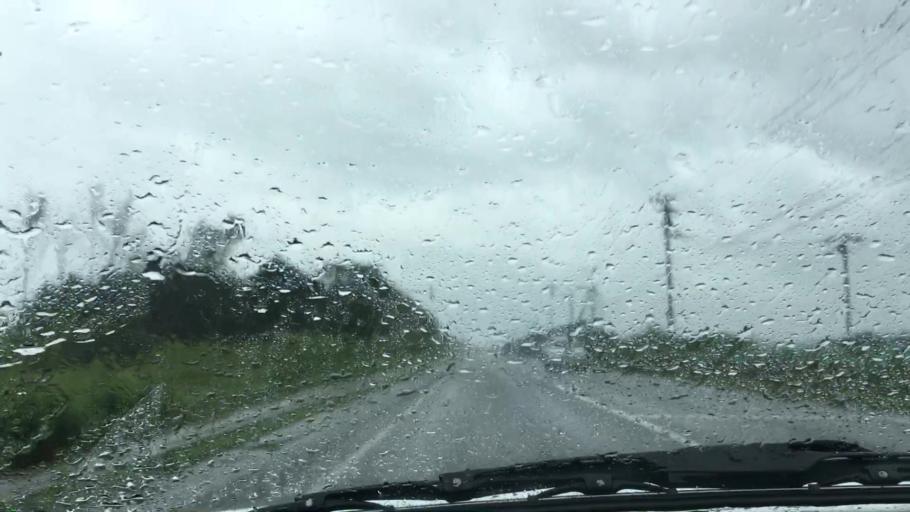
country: JP
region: Hokkaido
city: Nanae
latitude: 42.3124
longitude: 140.2734
